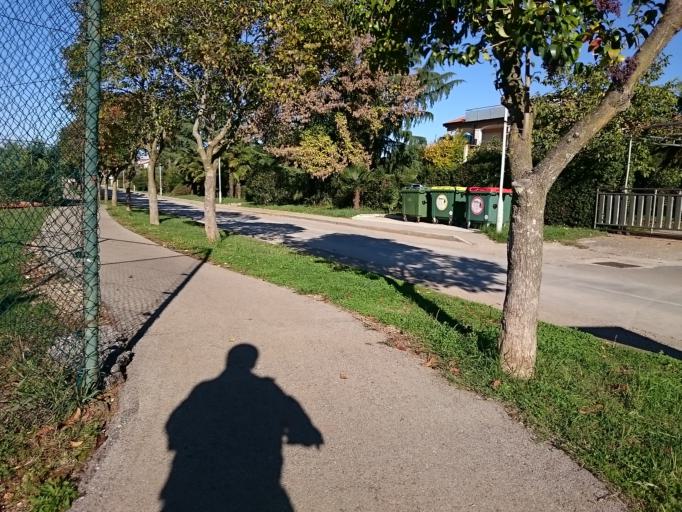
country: HR
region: Istarska
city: Novigrad
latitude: 45.3239
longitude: 13.5610
